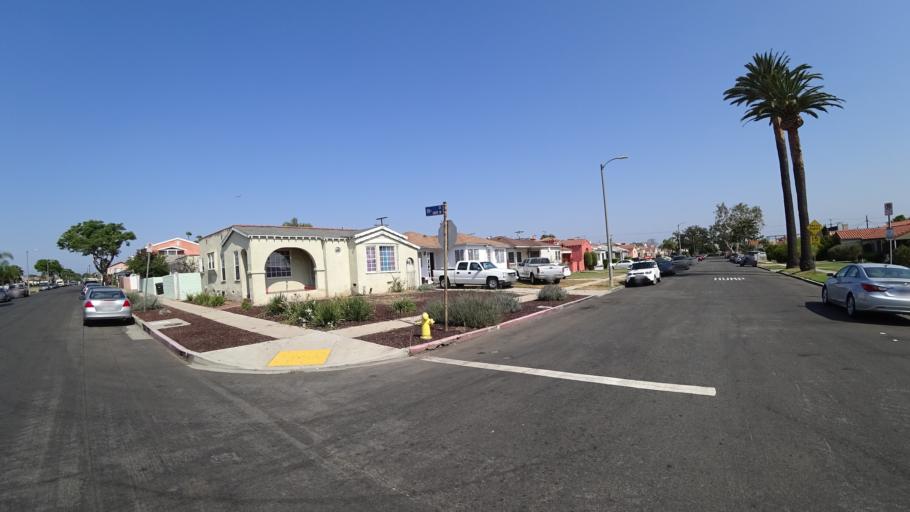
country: US
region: California
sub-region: Los Angeles County
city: Westmont
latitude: 33.9546
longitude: -118.3101
